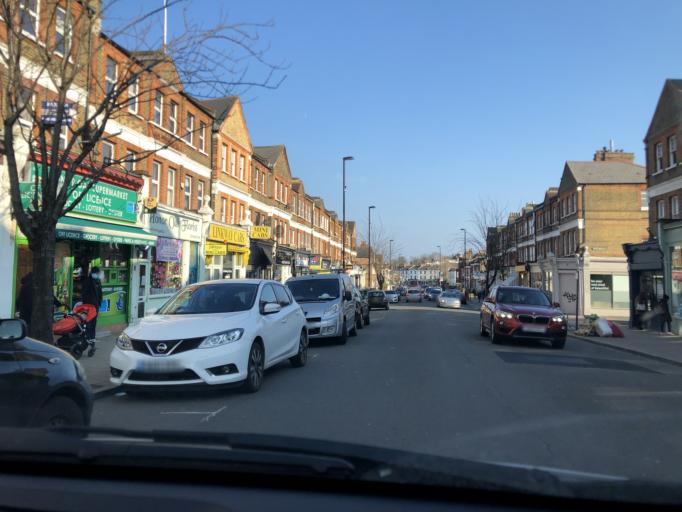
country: GB
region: England
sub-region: Greater London
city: Catford
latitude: 51.4494
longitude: -0.0446
